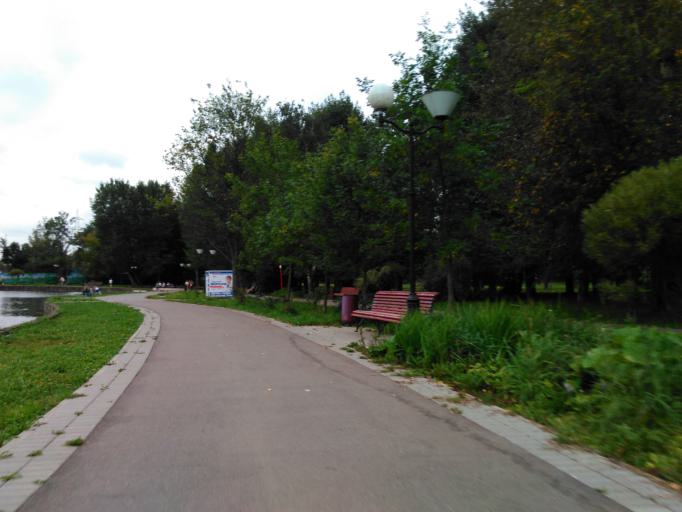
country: RU
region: Moscow
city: Kotlovka
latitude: 55.6479
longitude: 37.5873
